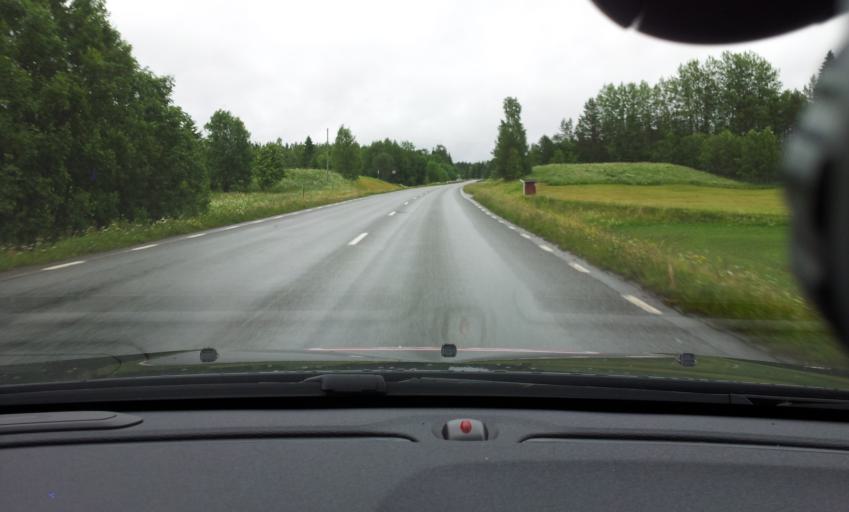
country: SE
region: Jaemtland
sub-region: Krokoms Kommun
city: Krokom
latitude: 63.3559
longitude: 14.4879
